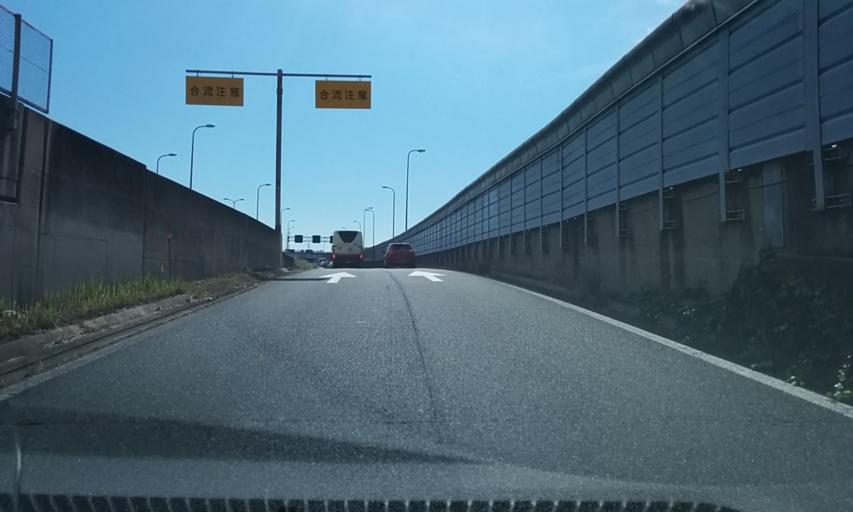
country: JP
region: Osaka
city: Ikeda
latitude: 34.8041
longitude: 135.4336
